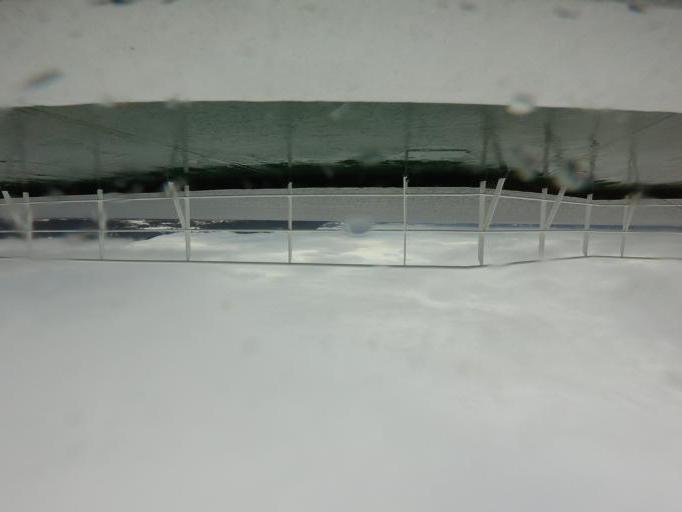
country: NO
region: Sor-Trondelag
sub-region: Skaun
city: Borsa
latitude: 63.4722
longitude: 10.1054
